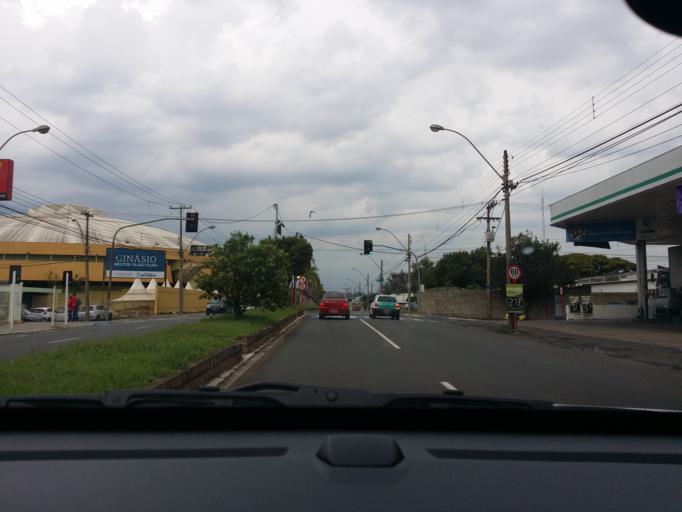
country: BR
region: Sao Paulo
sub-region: Sao Carlos
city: Sao Carlos
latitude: -22.0340
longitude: -47.8774
